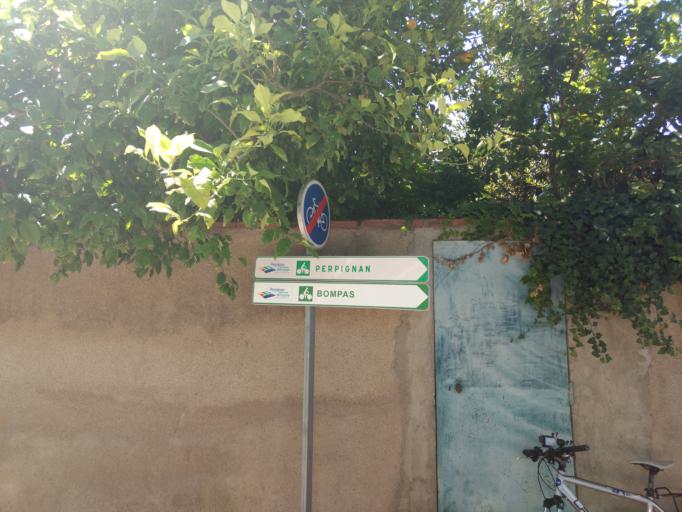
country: FR
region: Languedoc-Roussillon
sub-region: Departement des Pyrenees-Orientales
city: Sainte-Marie-Plage
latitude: 42.7283
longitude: 3.0154
